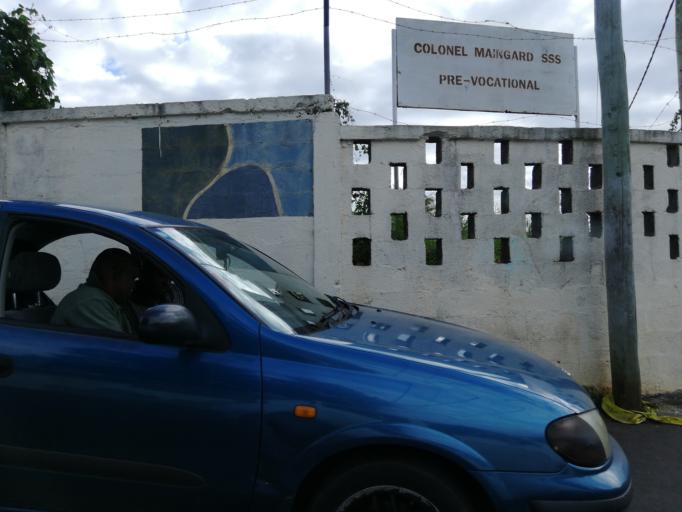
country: MU
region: Black River
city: Petite Riviere
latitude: -20.2215
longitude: 57.4611
